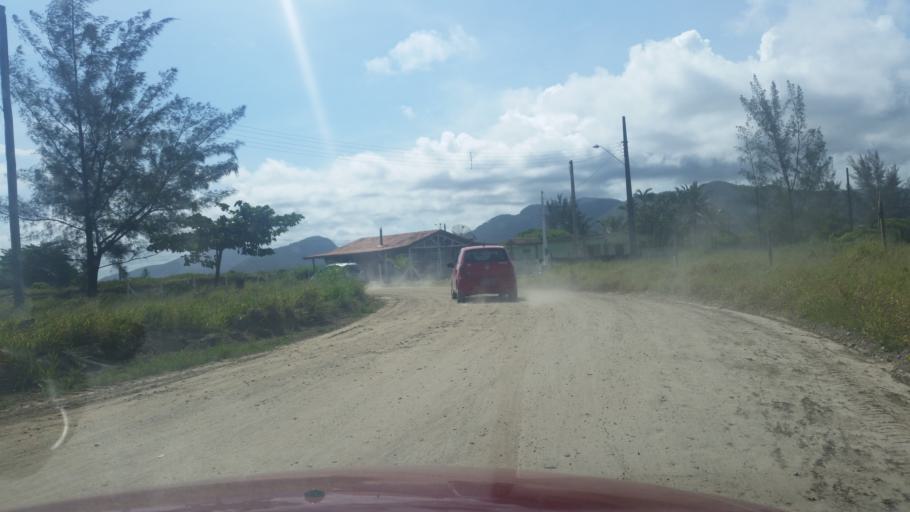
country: BR
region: Sao Paulo
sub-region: Iguape
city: Iguape
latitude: -24.6972
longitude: -47.4543
